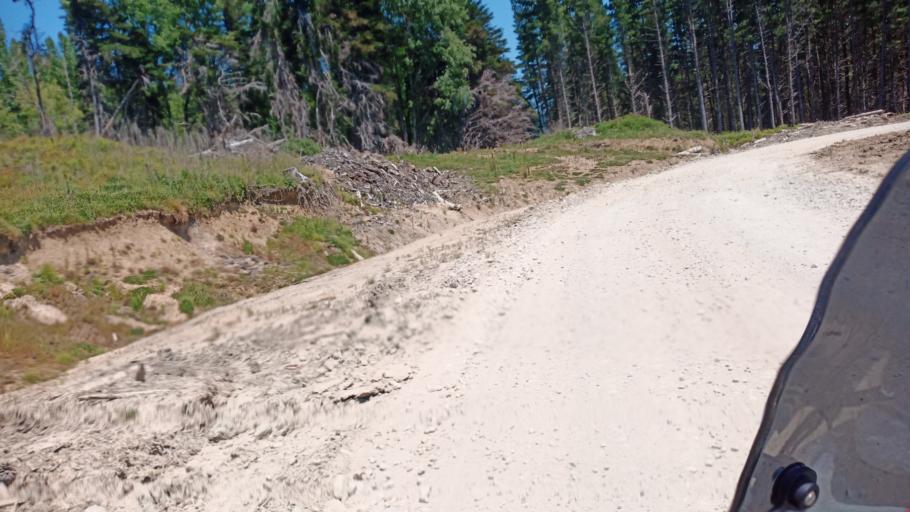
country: NZ
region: Gisborne
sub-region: Gisborne District
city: Gisborne
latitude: -38.2864
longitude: 178.0059
